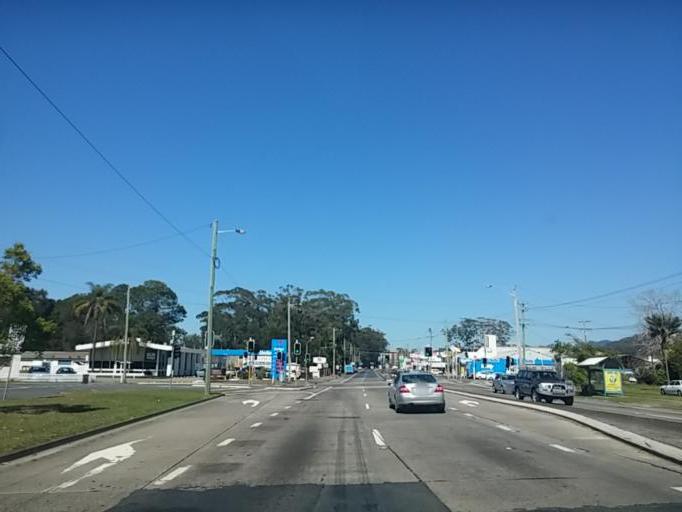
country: AU
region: New South Wales
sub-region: Coffs Harbour
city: Coffs Harbour
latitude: -30.2895
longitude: 153.1218
